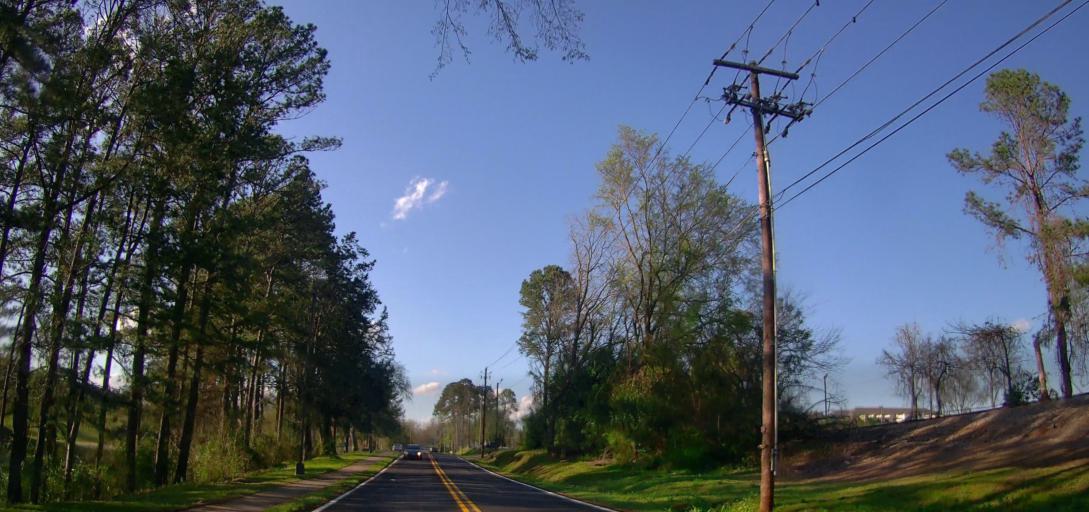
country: US
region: Georgia
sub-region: Baldwin County
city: Milledgeville
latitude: 33.0755
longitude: -83.2360
